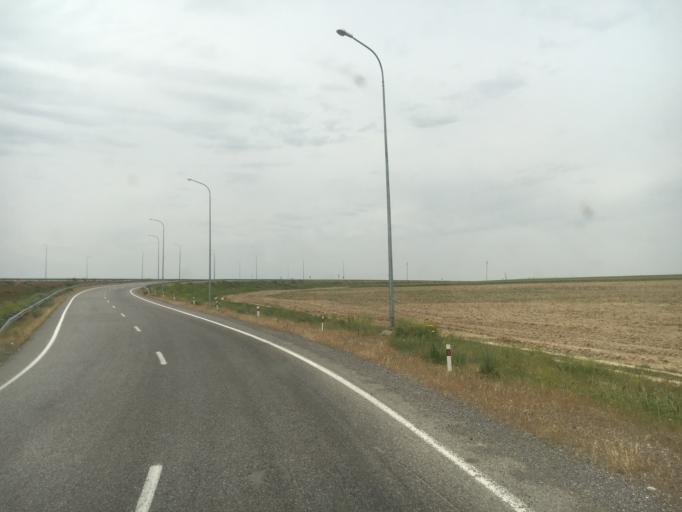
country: KZ
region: Ongtustik Qazaqstan
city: Temirlanovka
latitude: 42.5305
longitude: 69.3451
